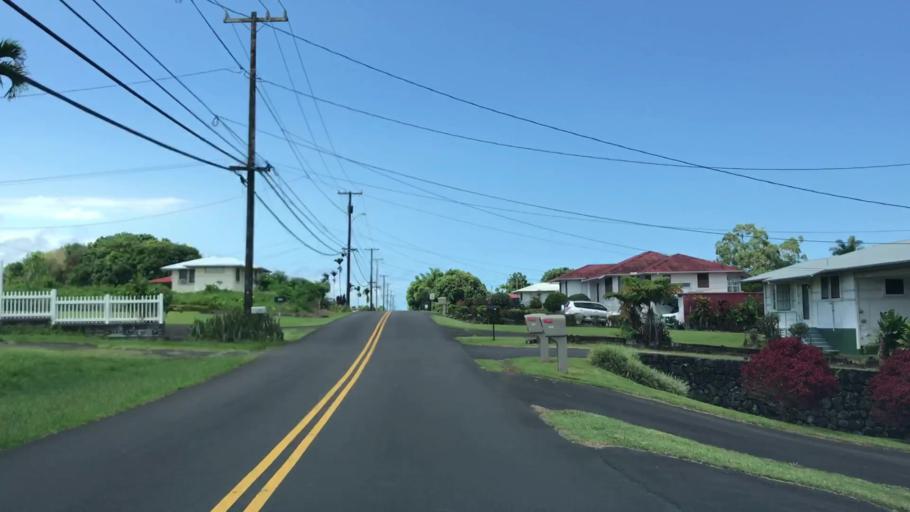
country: US
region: Hawaii
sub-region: Hawaii County
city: Hilo
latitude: 19.6773
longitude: -155.0800
